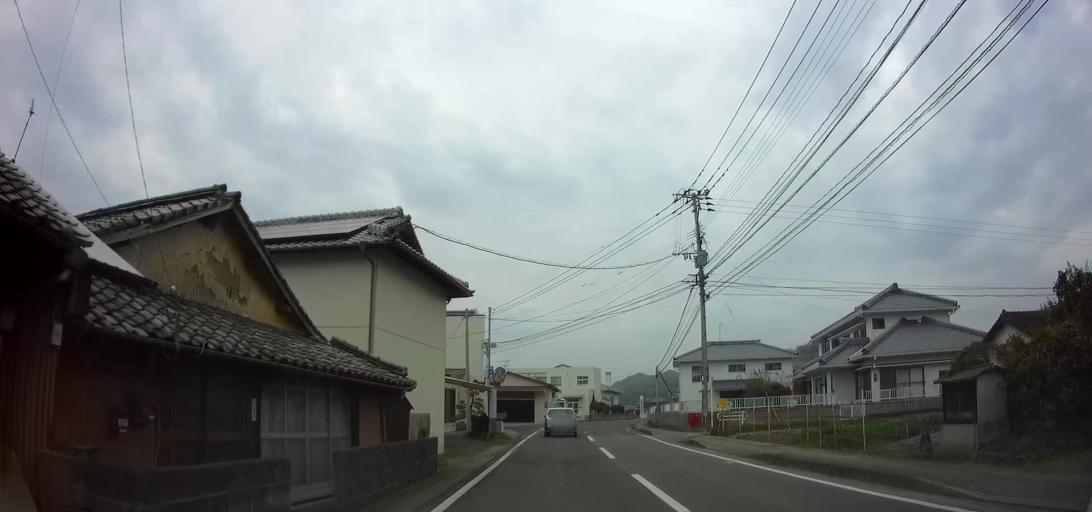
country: JP
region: Nagasaki
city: Shimabara
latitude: 32.6551
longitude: 130.2601
